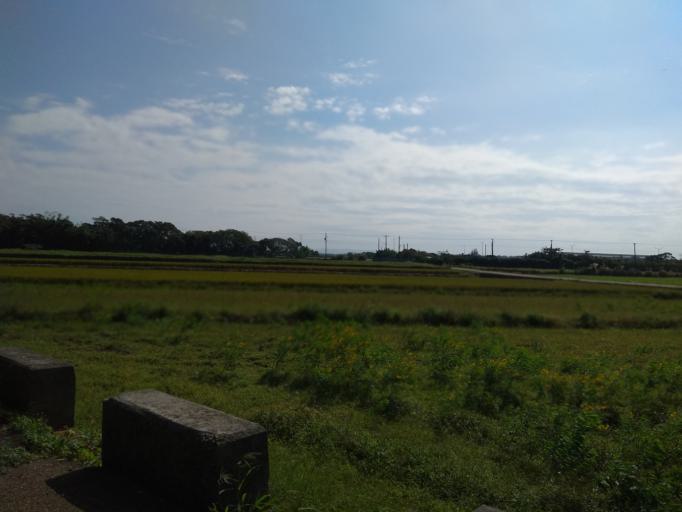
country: TW
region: Taiwan
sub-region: Hsinchu
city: Zhubei
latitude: 24.9480
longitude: 121.0054
